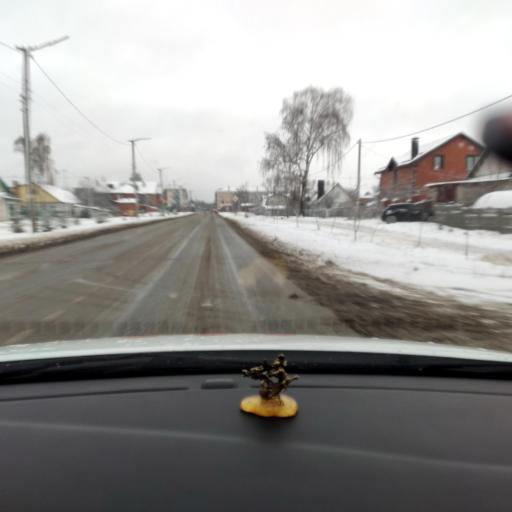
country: RU
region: Tatarstan
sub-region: Zelenodol'skiy Rayon
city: Zelenodolsk
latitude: 55.8531
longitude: 48.5305
